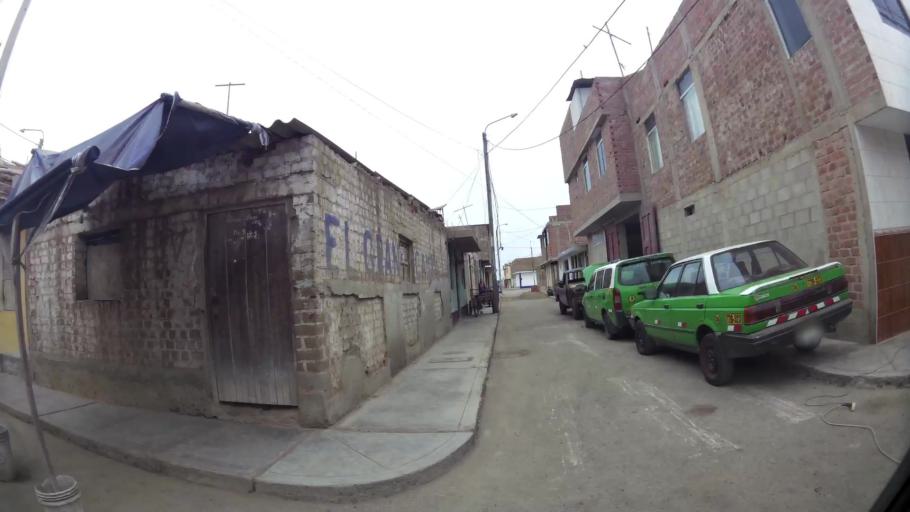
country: PE
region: La Libertad
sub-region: Provincia de Trujillo
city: Buenos Aires
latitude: -8.1486
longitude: -79.0459
